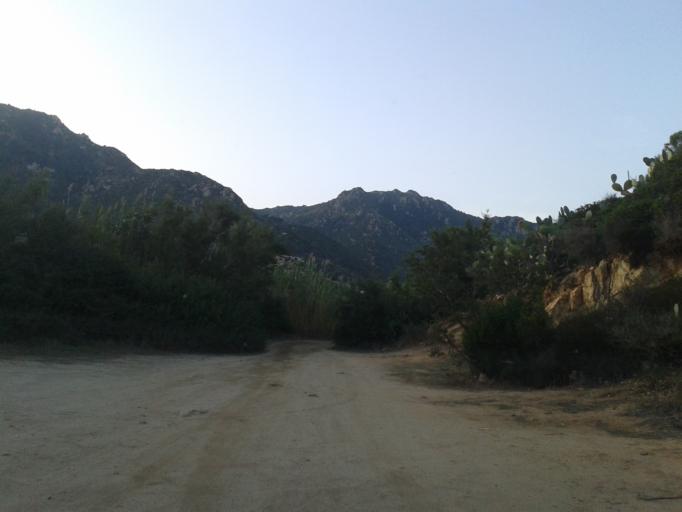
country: IT
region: Sardinia
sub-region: Provincia di Cagliari
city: Villasimius
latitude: 39.1355
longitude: 9.4891
